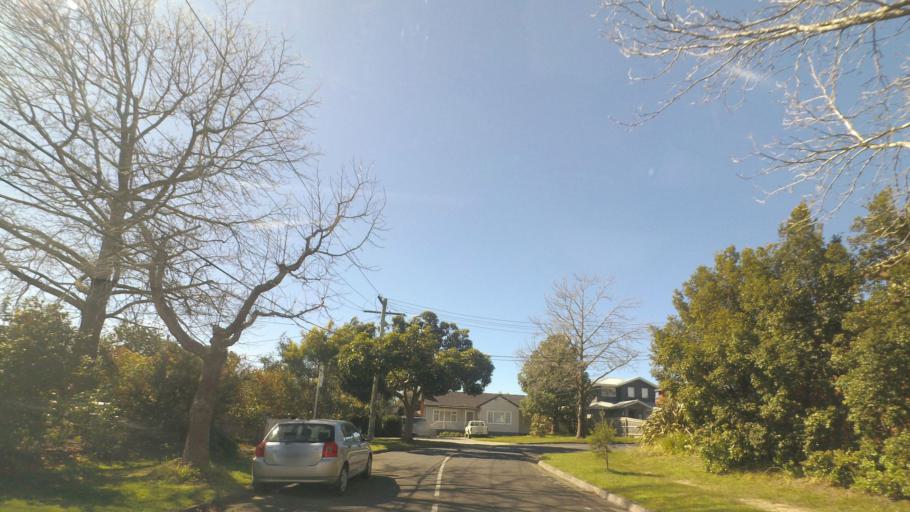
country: AU
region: Victoria
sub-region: Maroondah
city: Ringwood East
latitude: -37.8158
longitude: 145.2431
